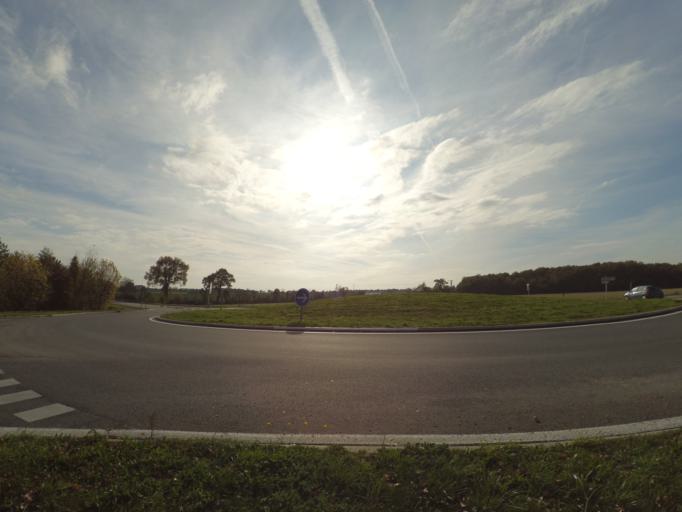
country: FR
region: Pays de la Loire
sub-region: Departement de la Vendee
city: Saint-Hilaire-de-Loulay
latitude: 47.0177
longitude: -1.3431
